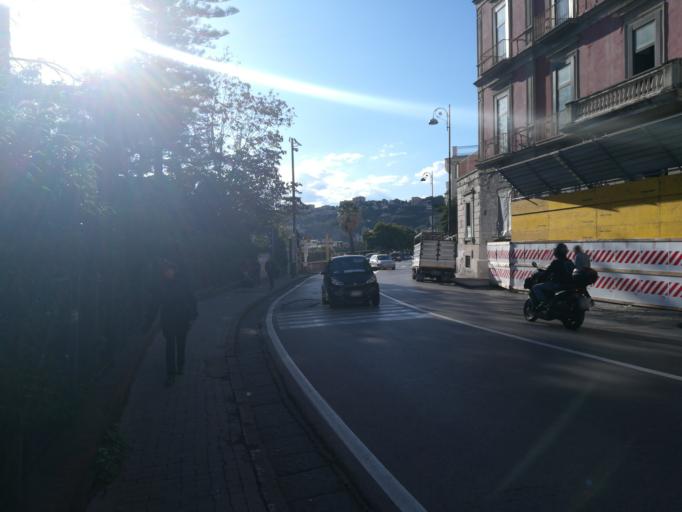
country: IT
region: Campania
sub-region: Provincia di Napoli
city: Napoli
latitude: 40.8369
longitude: 14.2298
